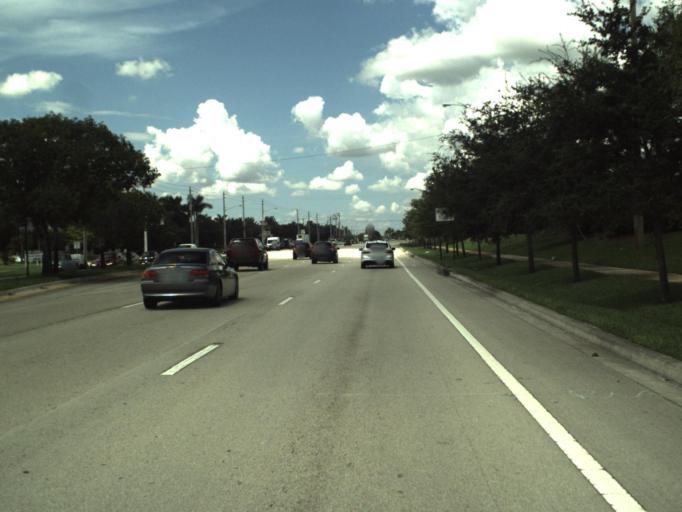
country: US
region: Florida
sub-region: Miami-Dade County
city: Country Club
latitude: 25.9788
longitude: -80.3056
